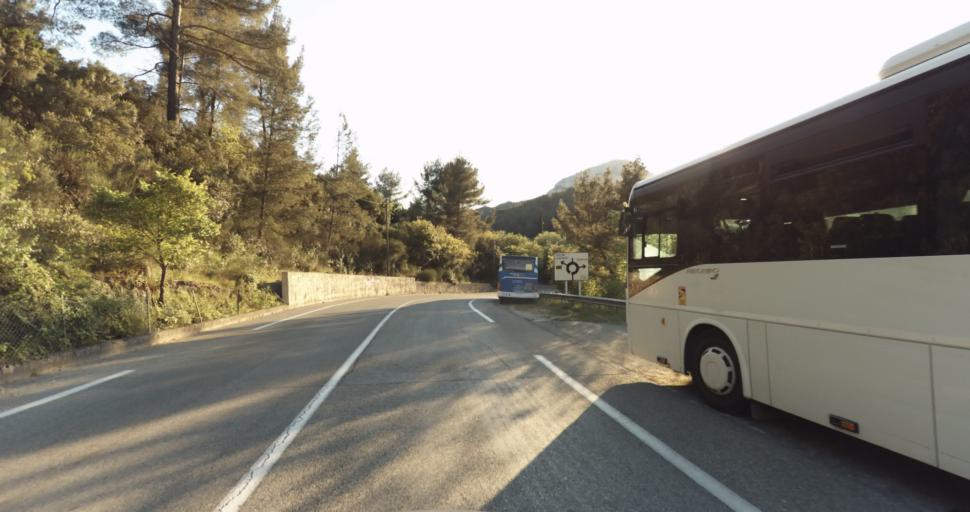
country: FR
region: Provence-Alpes-Cote d'Azur
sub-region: Departement du Var
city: Le Revest-les-Eaux
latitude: 43.1631
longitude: 5.9289
